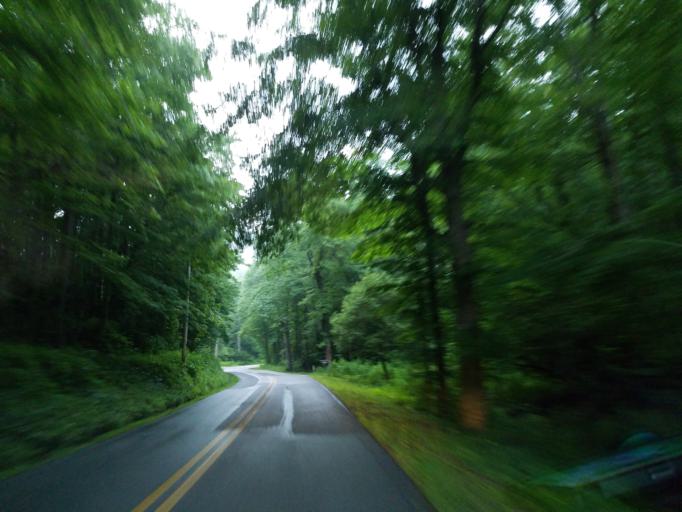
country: US
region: Georgia
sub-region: Lumpkin County
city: Dahlonega
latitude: 34.6625
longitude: -84.0343
